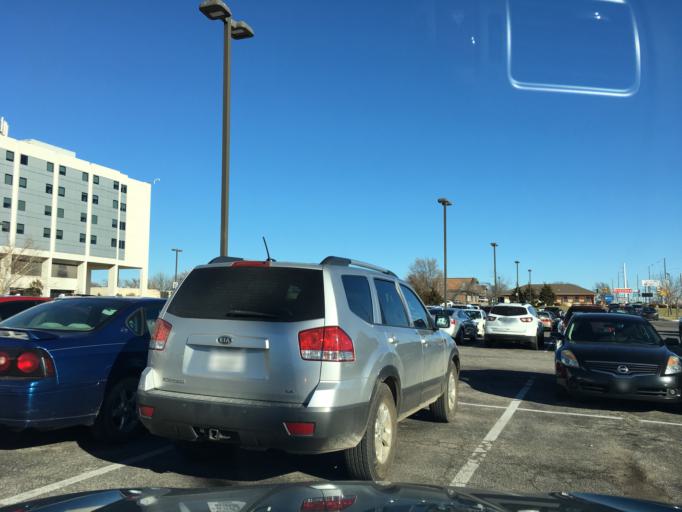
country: US
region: Kansas
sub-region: Sedgwick County
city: Wichita
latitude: 37.6650
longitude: -97.2934
